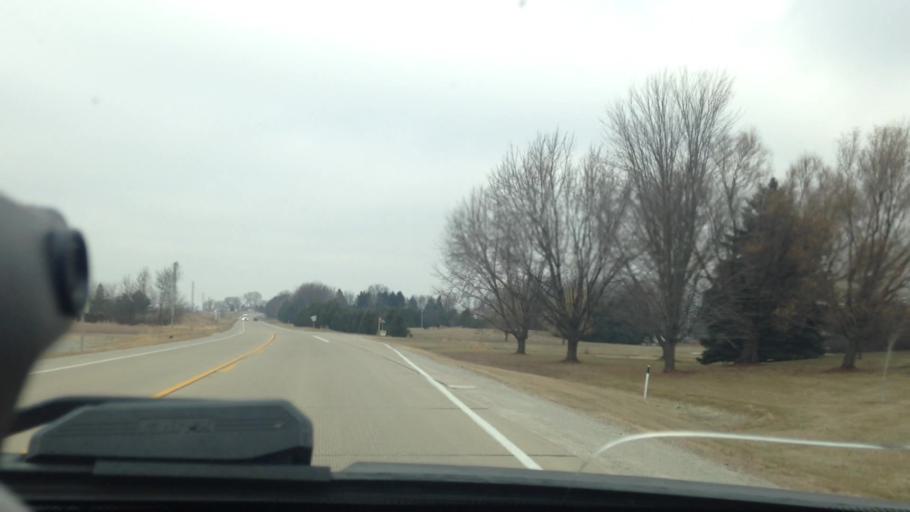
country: US
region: Wisconsin
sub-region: Dodge County
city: Beaver Dam
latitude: 43.4685
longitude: -88.7709
